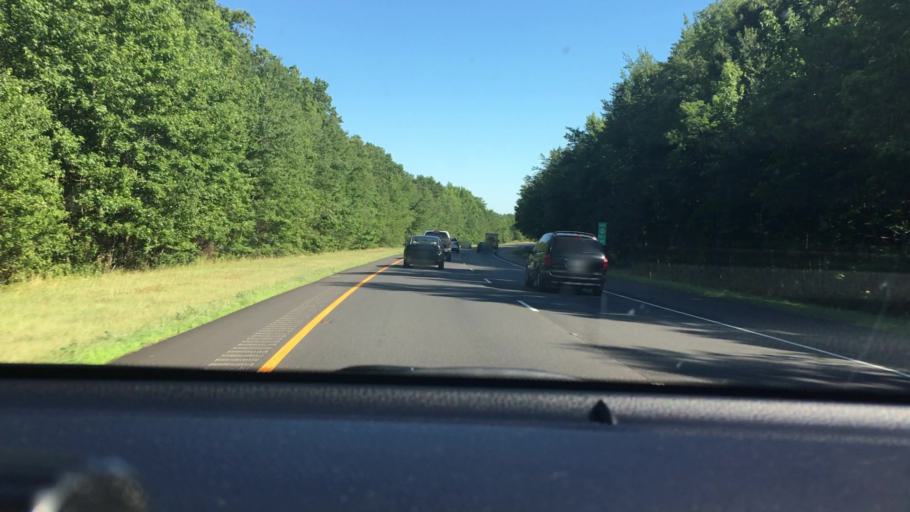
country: US
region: New Jersey
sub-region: Gloucester County
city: Glassboro
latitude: 39.6888
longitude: -75.1369
